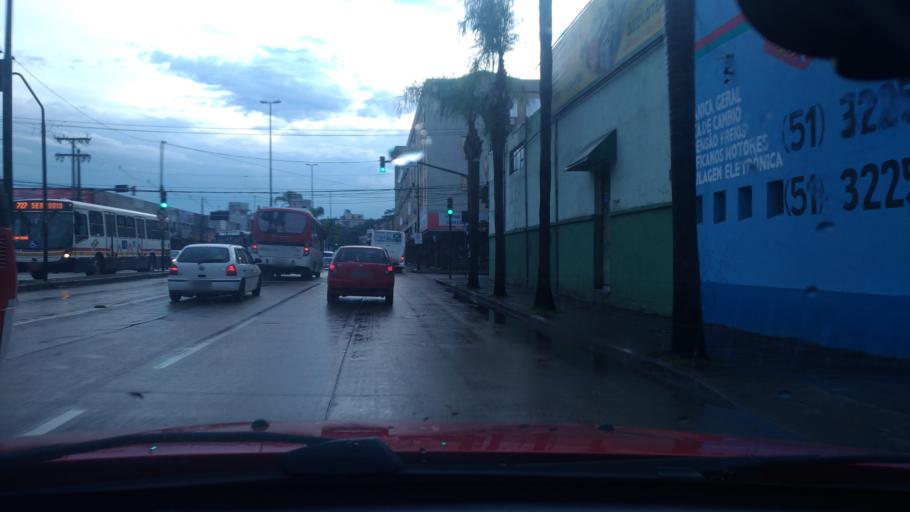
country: BR
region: Rio Grande do Sul
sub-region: Porto Alegre
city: Porto Alegre
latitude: -30.0224
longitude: -51.2124
